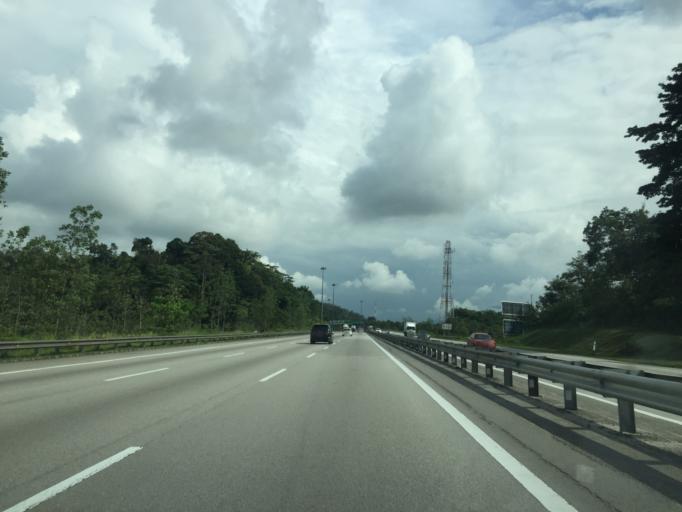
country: MY
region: Selangor
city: Batang Berjuntai
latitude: 3.5715
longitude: 101.5236
